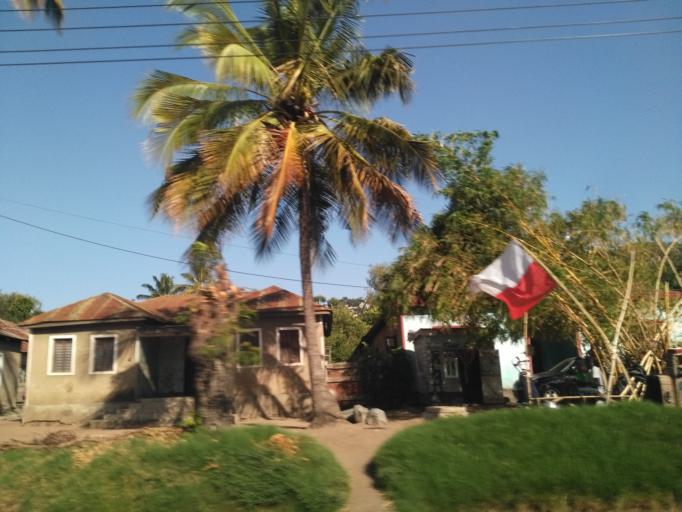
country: TZ
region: Mwanza
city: Mwanza
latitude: -2.5014
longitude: 32.8962
